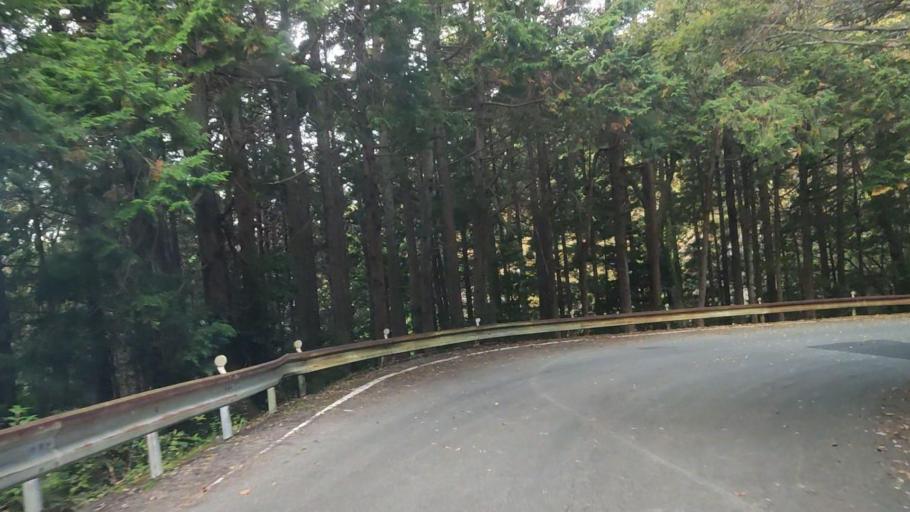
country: JP
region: Shizuoka
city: Ito
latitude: 34.9529
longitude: 139.0533
